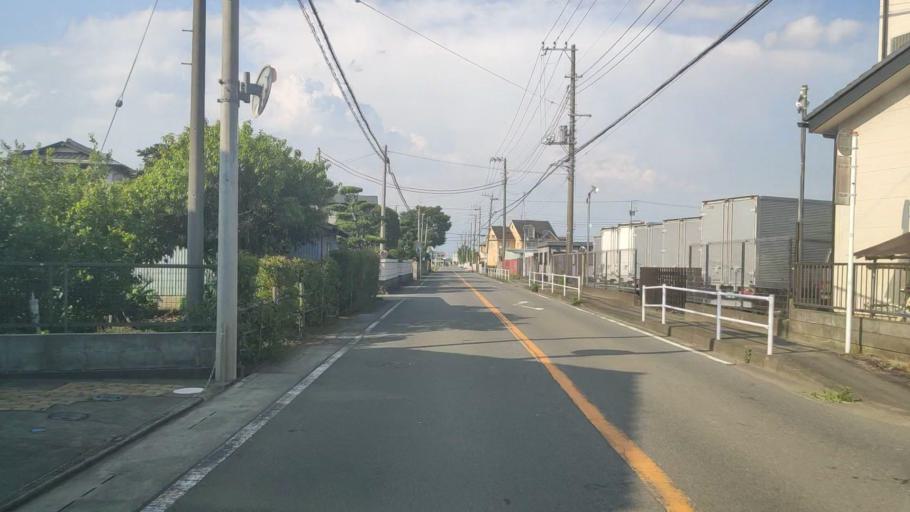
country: JP
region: Kanagawa
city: Isehara
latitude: 35.3771
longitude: 139.3348
